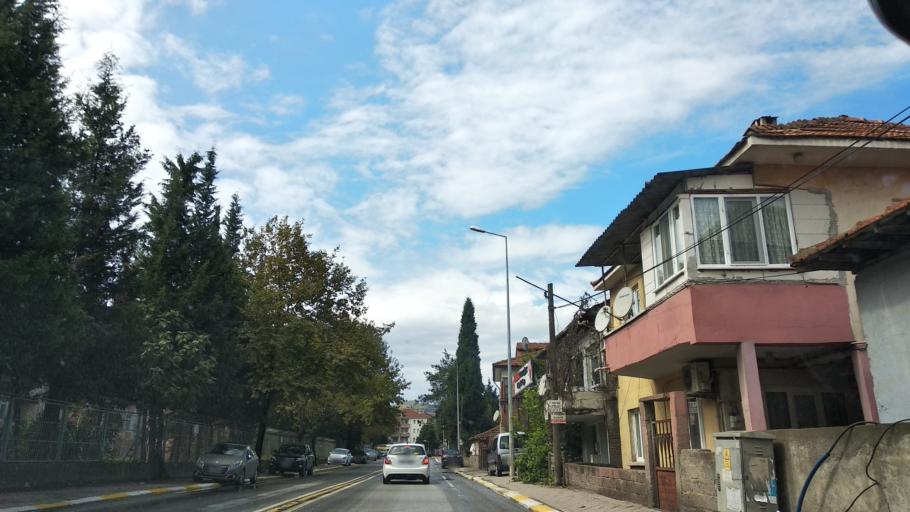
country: TR
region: Sakarya
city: Adapazari
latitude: 40.7579
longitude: 30.3711
